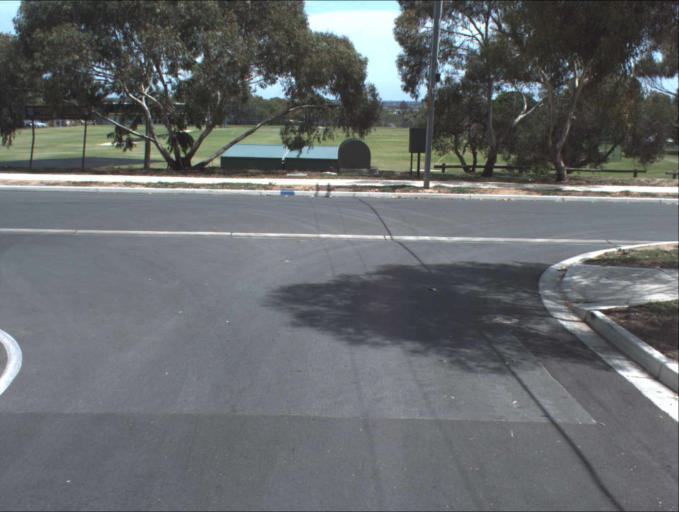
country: AU
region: South Australia
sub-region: Port Adelaide Enfield
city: Enfield
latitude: -34.8519
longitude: 138.6154
